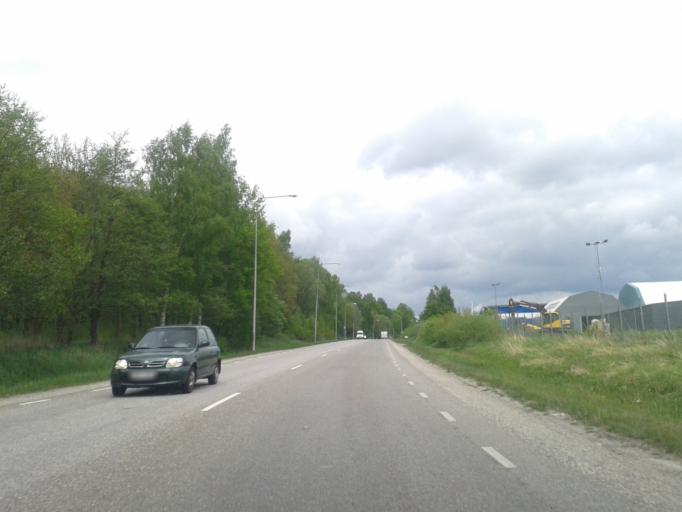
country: SE
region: Vaestra Goetaland
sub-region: Goteborg
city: Eriksbo
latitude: 57.7759
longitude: 12.0483
